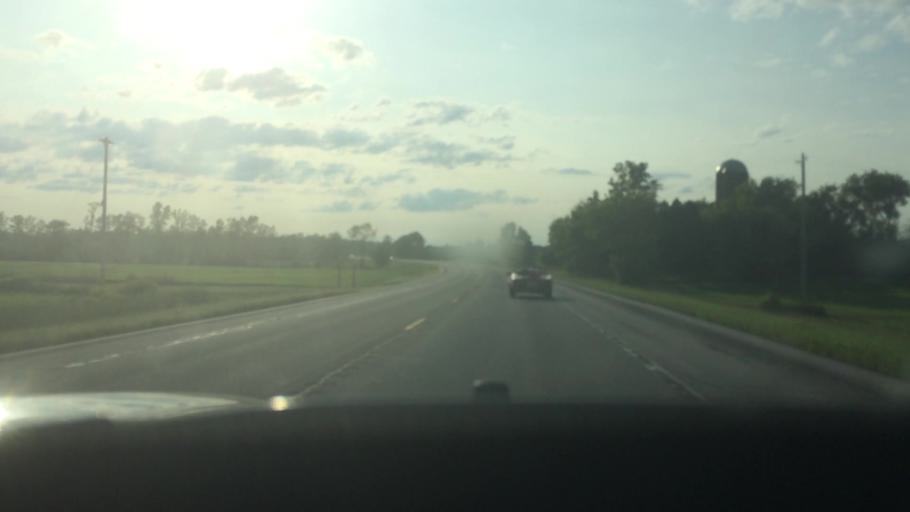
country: US
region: New York
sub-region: St. Lawrence County
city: Canton
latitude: 44.6351
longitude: -75.2594
